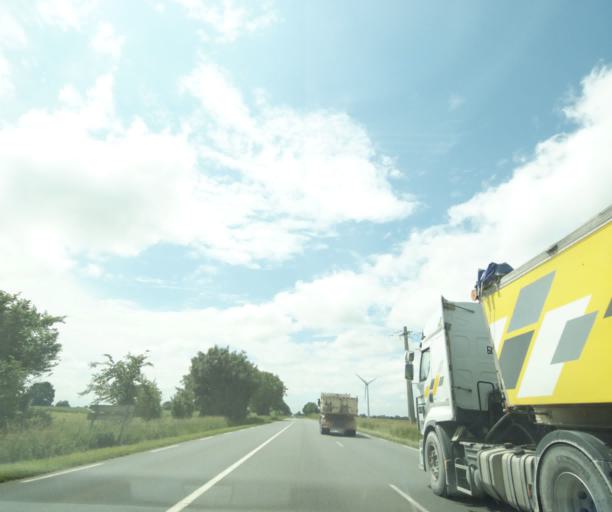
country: FR
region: Poitou-Charentes
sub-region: Departement des Deux-Sevres
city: Champdeniers-Saint-Denis
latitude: 46.4627
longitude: -0.3740
